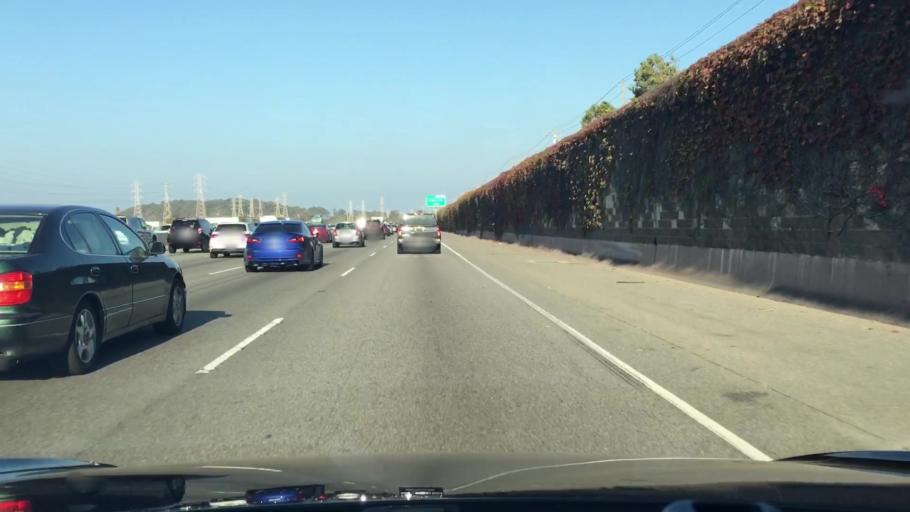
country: US
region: California
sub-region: San Mateo County
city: Burlingame
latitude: 37.5878
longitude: -122.3422
